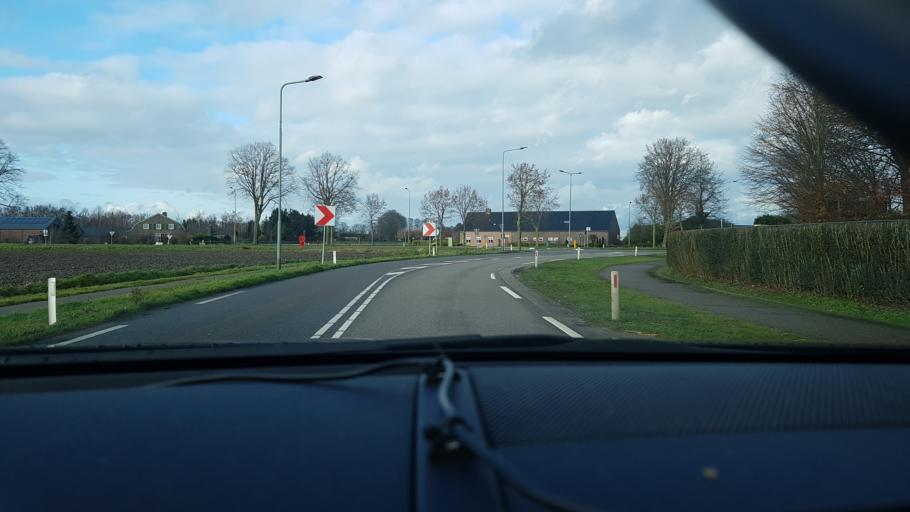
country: NL
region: Limburg
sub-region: Gemeente Nederweert
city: Nederweert
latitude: 51.2913
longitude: 5.7673
